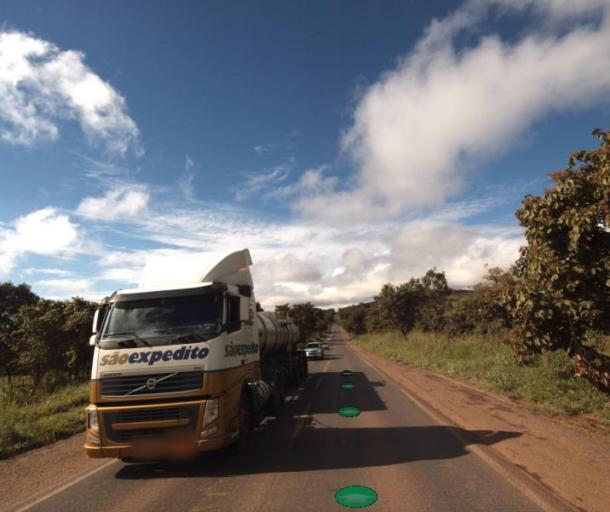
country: BR
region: Goias
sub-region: Uruacu
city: Uruacu
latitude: -14.5490
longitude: -49.1602
